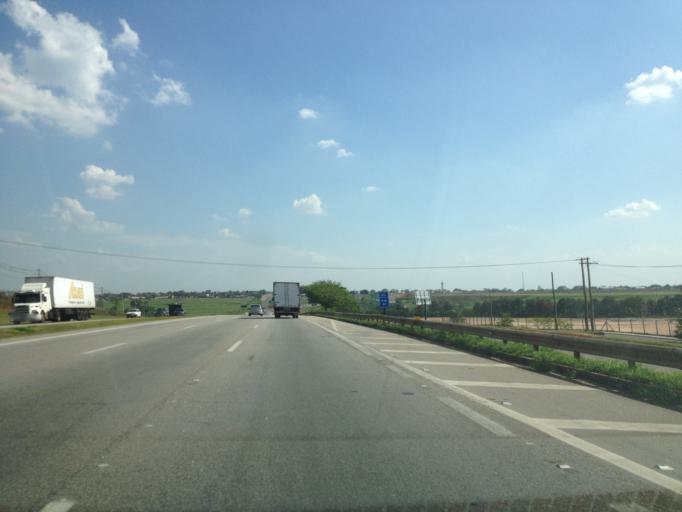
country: BR
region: Sao Paulo
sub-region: Campinas
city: Campinas
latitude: -23.0100
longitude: -47.1156
